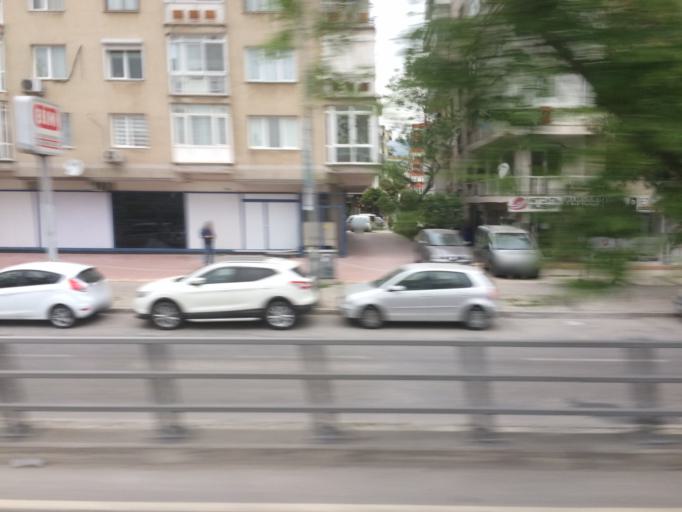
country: TR
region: Izmir
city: Bornova
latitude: 38.4552
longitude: 27.1992
